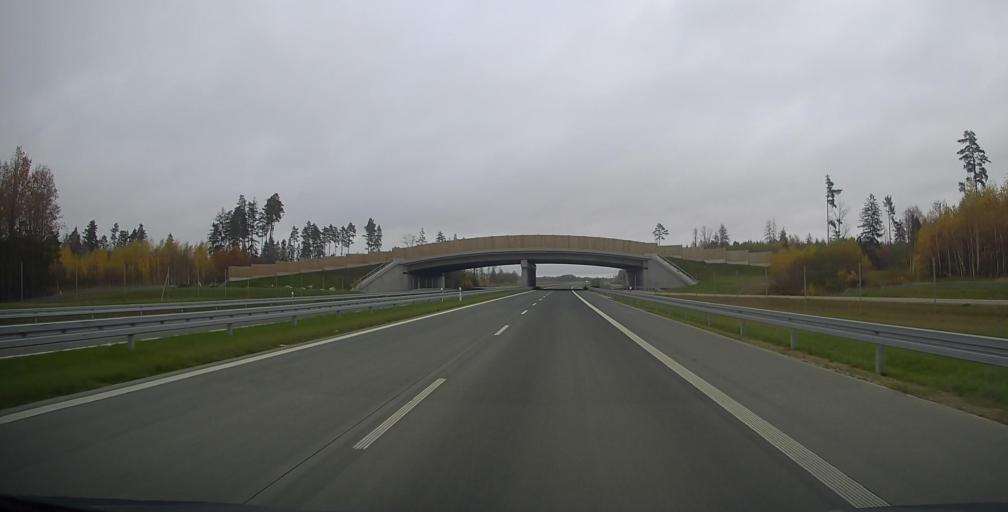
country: PL
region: Podlasie
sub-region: Powiat suwalski
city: Raczki
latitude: 53.8983
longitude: 22.6909
